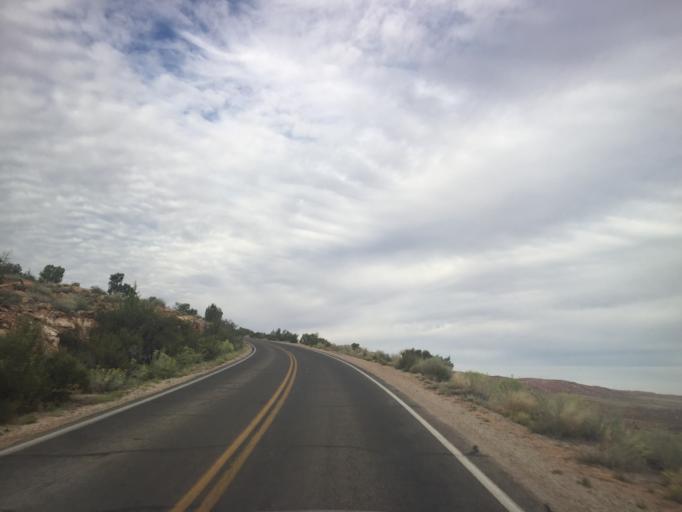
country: US
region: Utah
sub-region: Grand County
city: Moab
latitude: 38.7235
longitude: -109.5463
